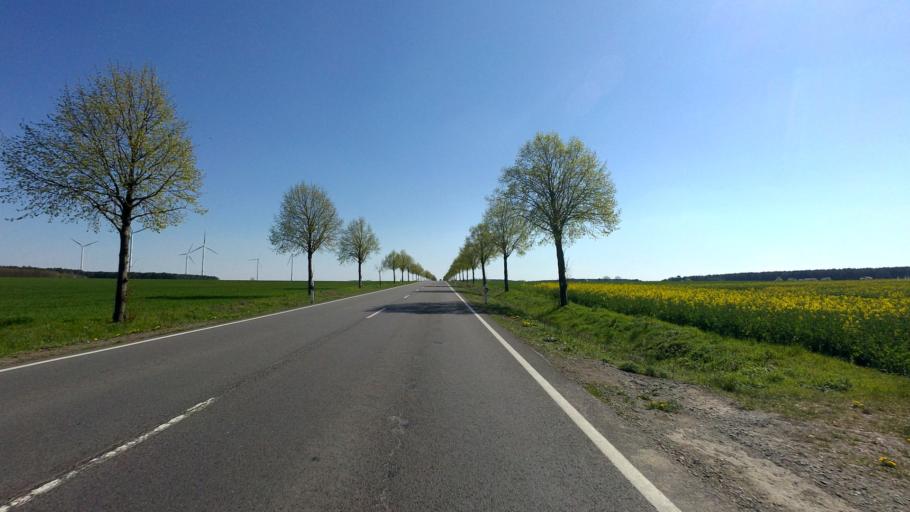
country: DE
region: Saxony-Anhalt
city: Pretzier
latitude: 52.7297
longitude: 11.2462
